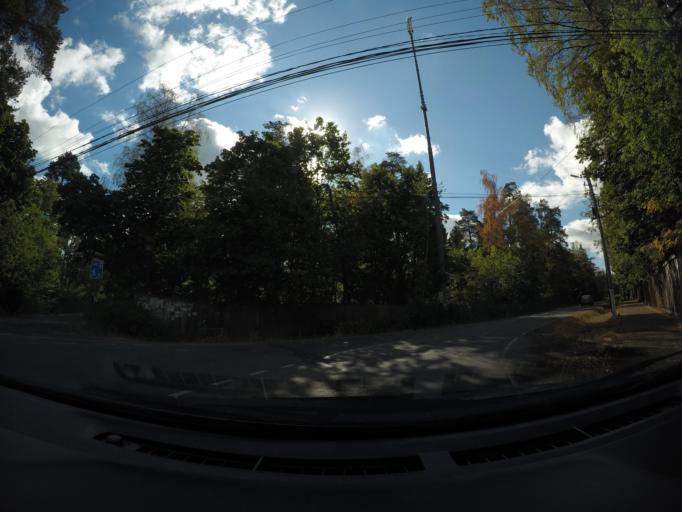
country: RU
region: Moskovskaya
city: Il'inskiy
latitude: 55.6110
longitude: 38.1370
